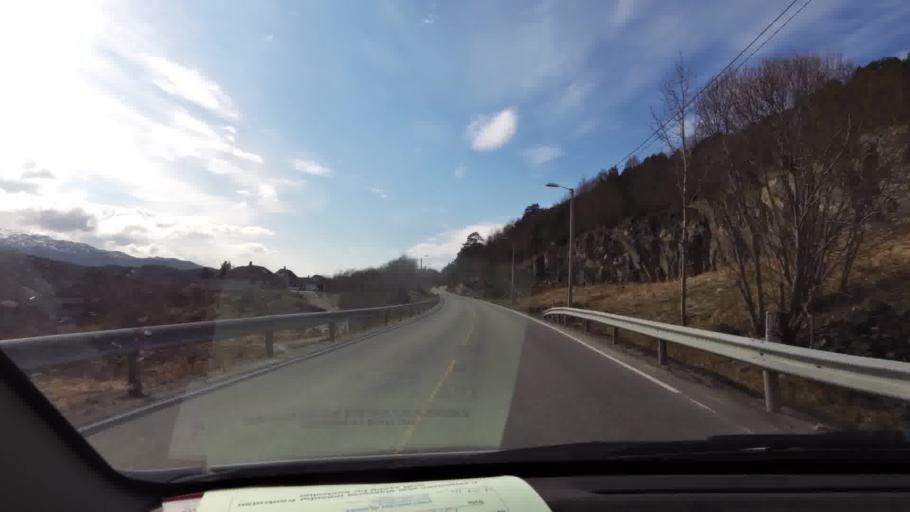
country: NO
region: More og Romsdal
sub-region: Kristiansund
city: Rensvik
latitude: 63.1093
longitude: 7.8522
